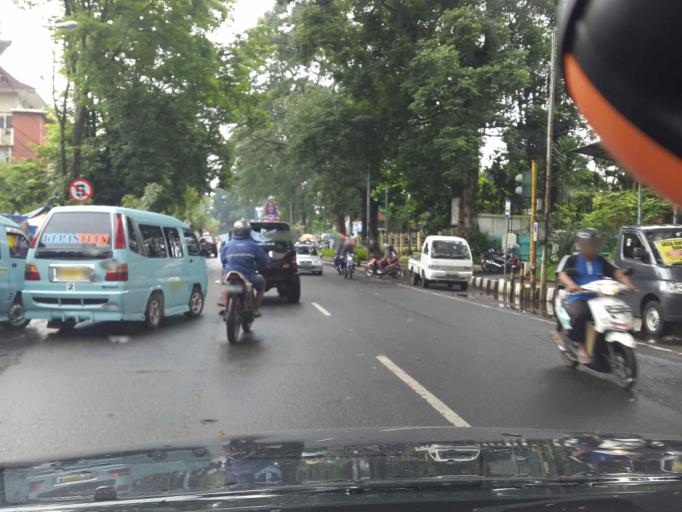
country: ID
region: Central Java
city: Salatiga
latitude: -7.3199
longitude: 110.4982
